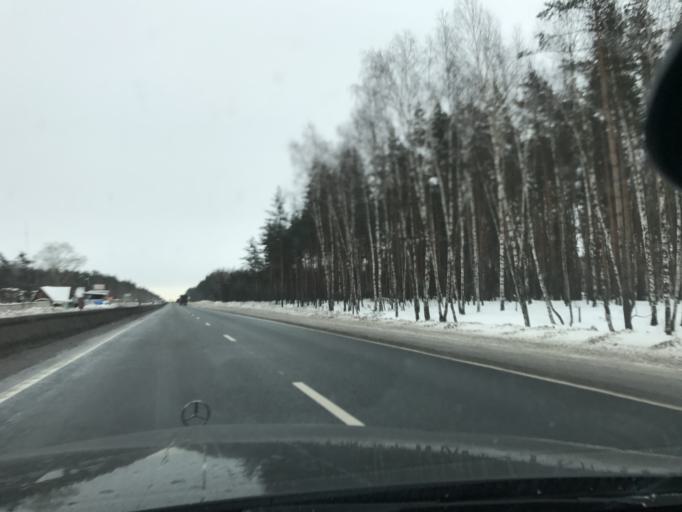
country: RU
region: Nizjnij Novgorod
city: Pyra
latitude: 56.2943
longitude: 43.3781
